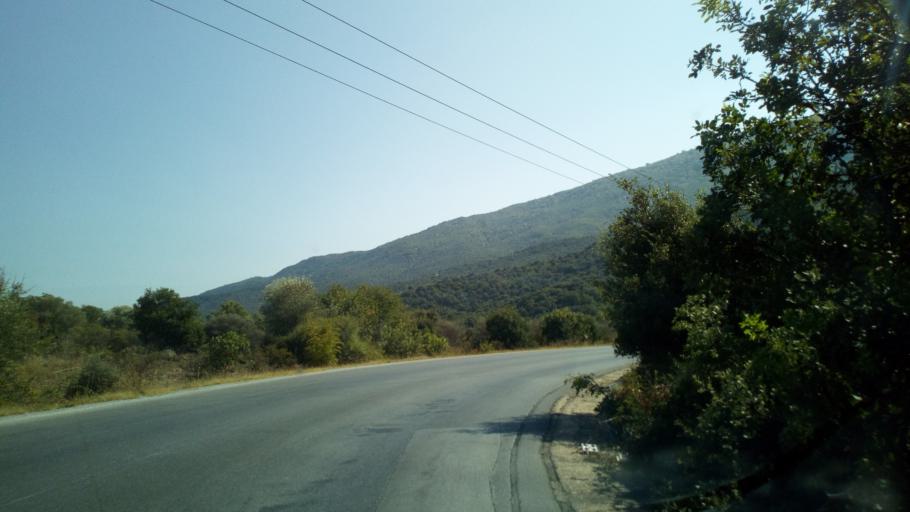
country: GR
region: Central Macedonia
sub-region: Nomos Thessalonikis
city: Stavros
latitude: 40.6494
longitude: 23.7458
